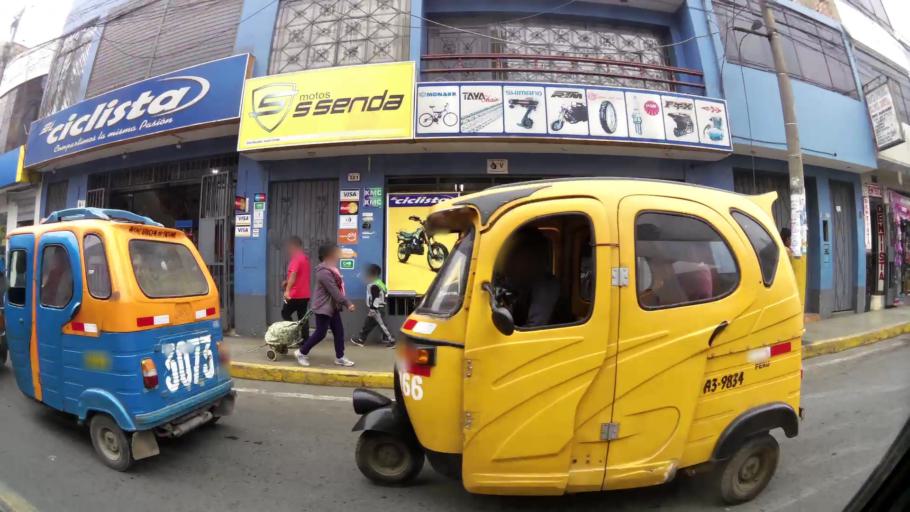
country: PE
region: Lima
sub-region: Barranca
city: Barranca
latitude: -10.7495
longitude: -77.7623
